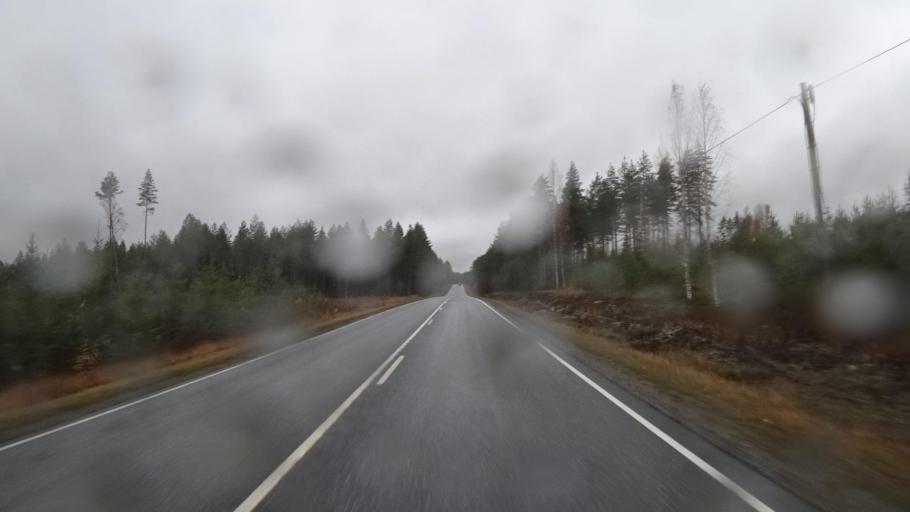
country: FI
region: Northern Savo
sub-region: Koillis-Savo
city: Tuusniemi
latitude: 62.8672
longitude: 28.3655
